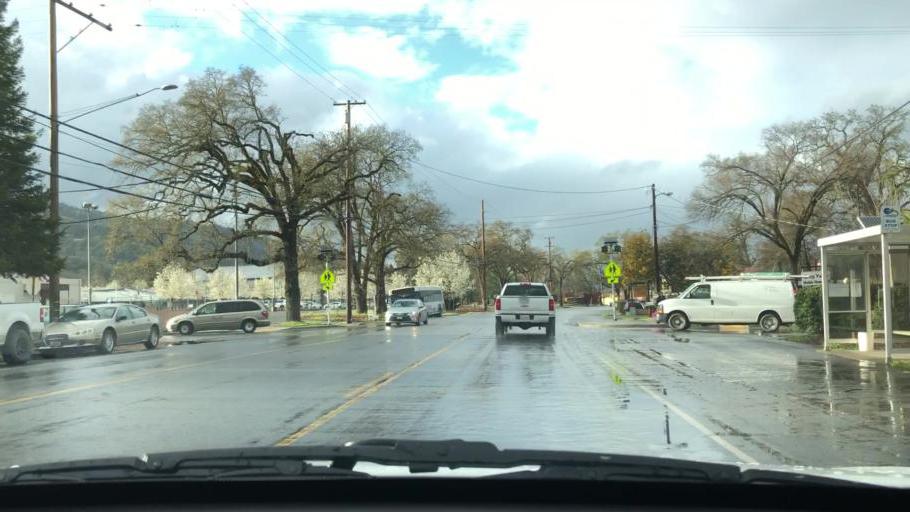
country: US
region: California
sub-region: Mendocino County
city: Ukiah
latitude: 39.1218
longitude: -123.2035
